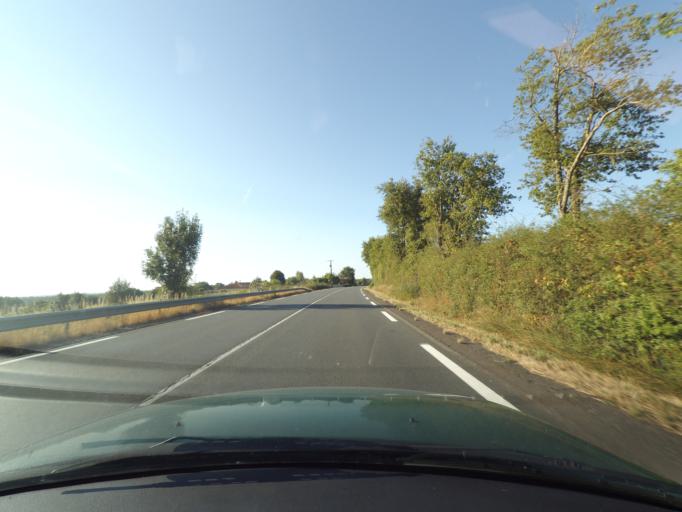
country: FR
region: Poitou-Charentes
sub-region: Departement des Deux-Sevres
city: Viennay
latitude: 46.7325
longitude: -0.2998
